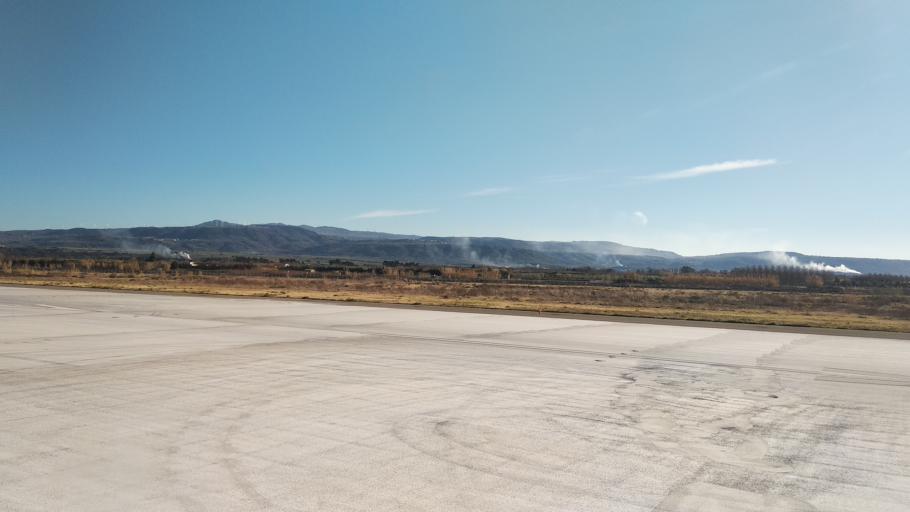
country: IT
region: Calabria
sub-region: Provincia di Catanzaro
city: Santa Eufemia Lamezia
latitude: 38.9034
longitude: 16.2614
